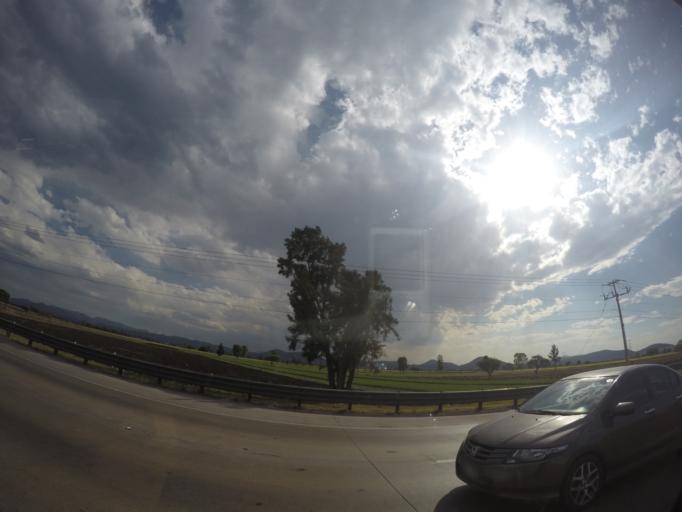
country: MX
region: Queretaro
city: El Sauz
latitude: 20.4682
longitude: -100.1044
